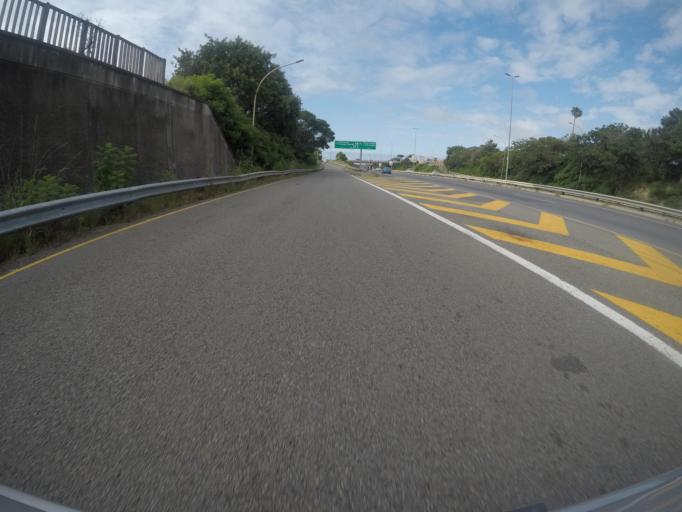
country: ZA
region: Eastern Cape
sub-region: Buffalo City Metropolitan Municipality
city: East London
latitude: -32.9912
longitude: 27.9191
